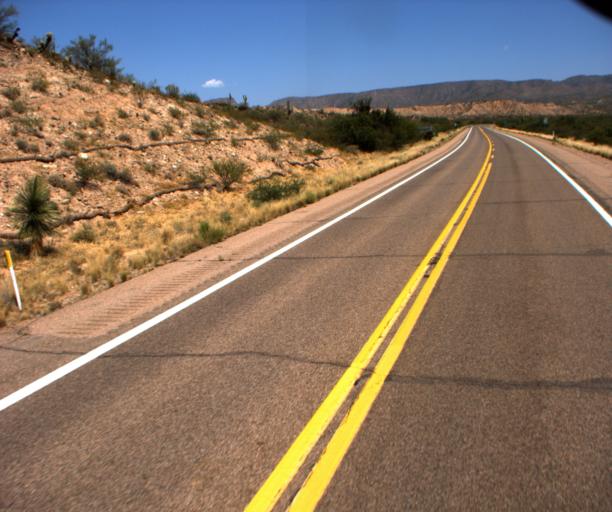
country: US
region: Arizona
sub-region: Gila County
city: Miami
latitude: 33.5961
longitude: -110.9958
